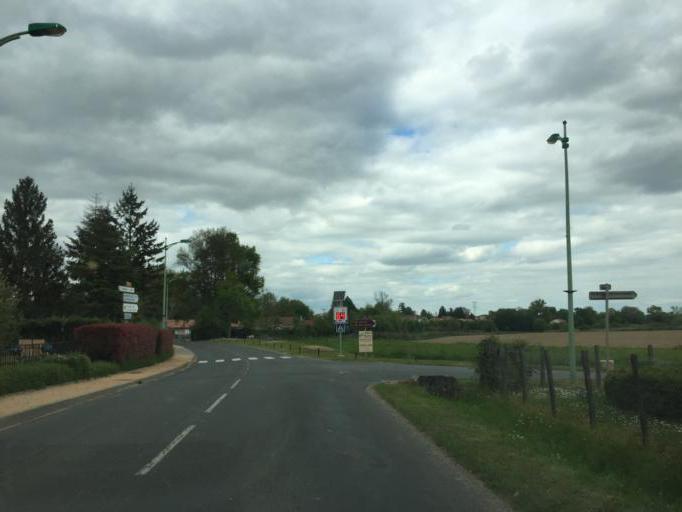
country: FR
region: Rhone-Alpes
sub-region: Departement de l'Ain
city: Saint-Andre-de-Corcy
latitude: 45.9528
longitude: 4.9402
